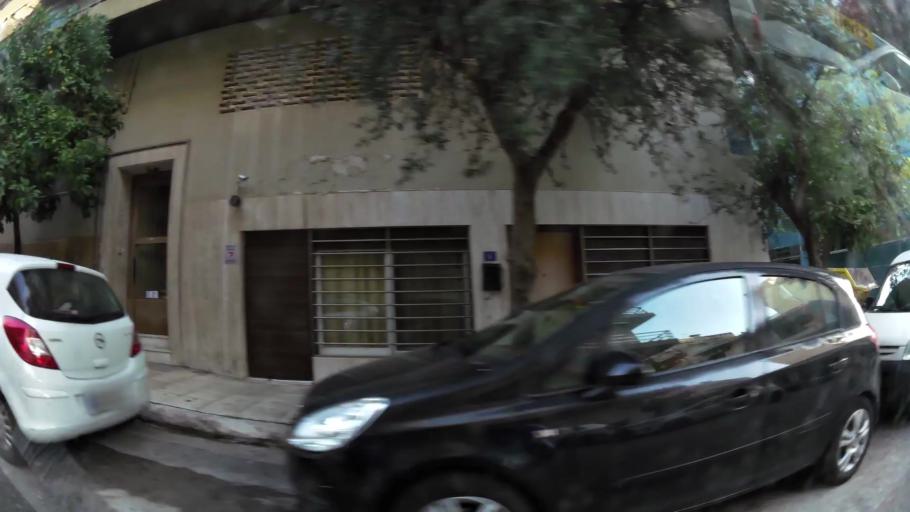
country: GR
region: Attica
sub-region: Nomarchia Athinas
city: Vyronas
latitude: 37.9732
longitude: 23.7555
